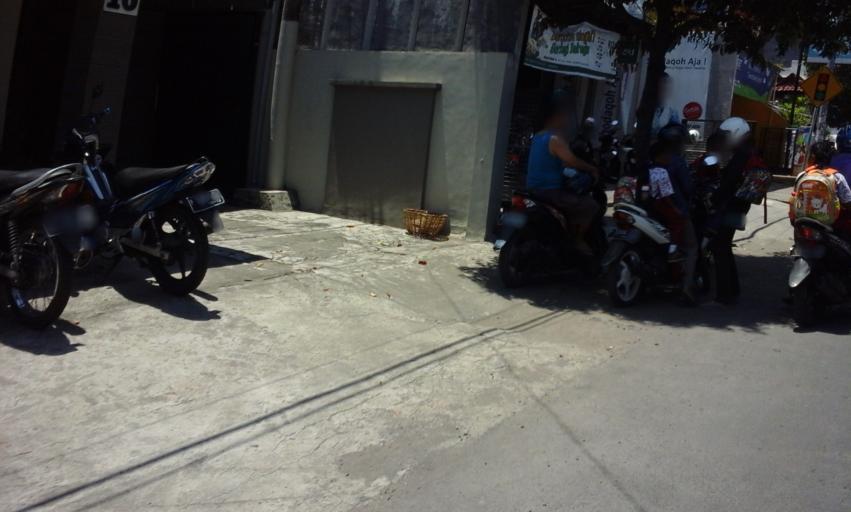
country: ID
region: East Java
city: Sumbersari Wetan
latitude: -8.1810
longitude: 113.7155
